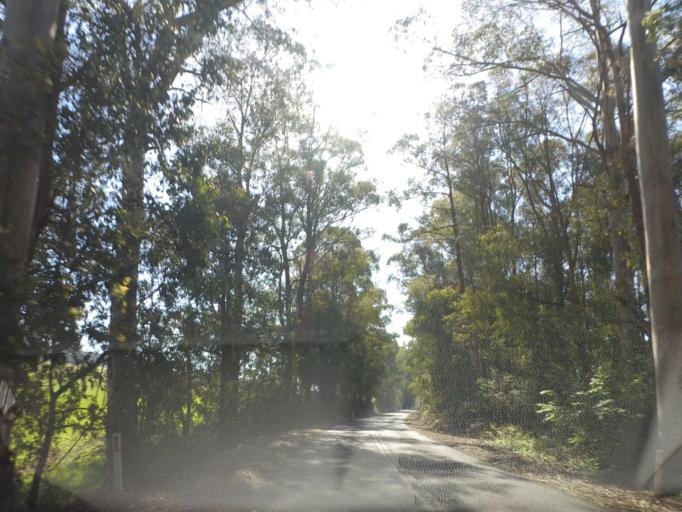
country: AU
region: Victoria
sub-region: Baw Baw
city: Warragul
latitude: -37.8937
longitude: 145.9474
